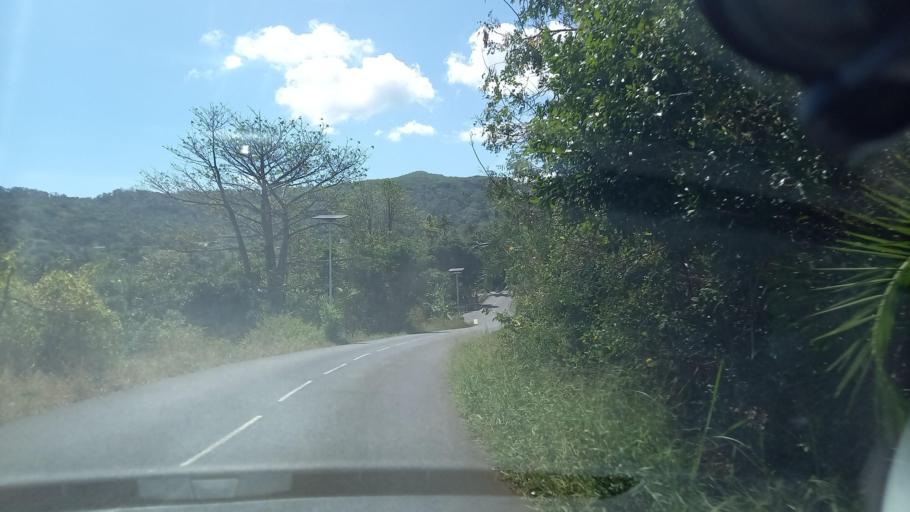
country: YT
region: Kani-Keli
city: Kani Keli
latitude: -12.9620
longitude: 45.1120
